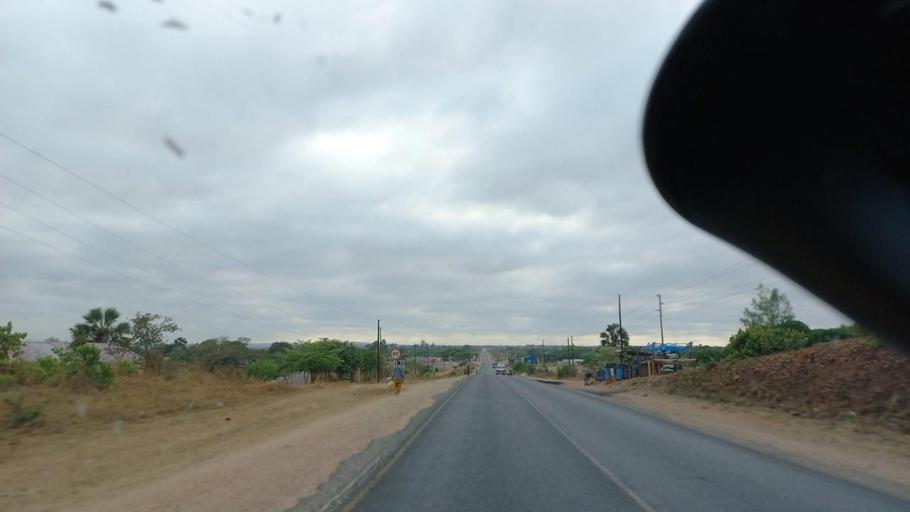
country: ZM
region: Lusaka
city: Chongwe
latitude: -15.3410
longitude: 28.6116
